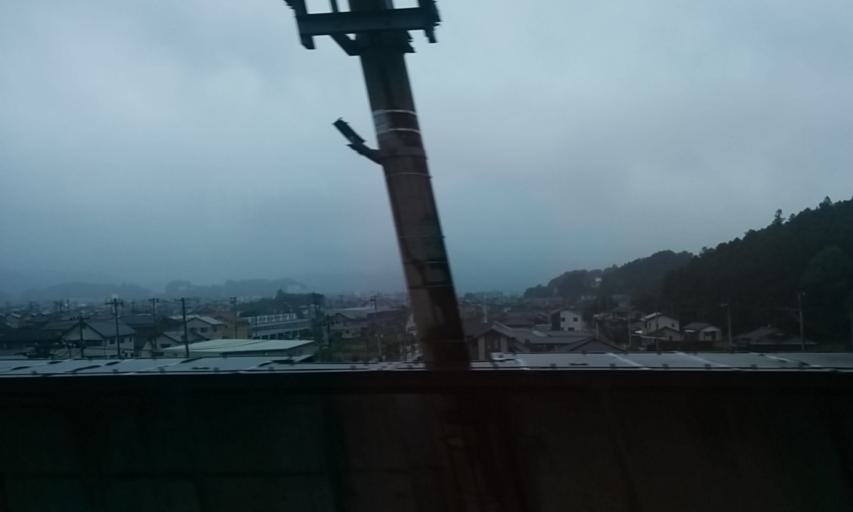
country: JP
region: Miyagi
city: Shiroishi
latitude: 37.9983
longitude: 140.6356
